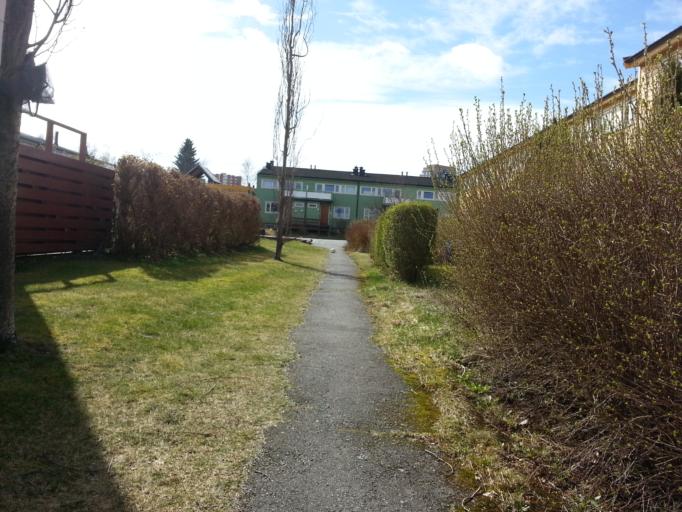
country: NO
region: Sor-Trondelag
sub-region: Trondheim
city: Trondheim
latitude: 63.4270
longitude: 10.4491
